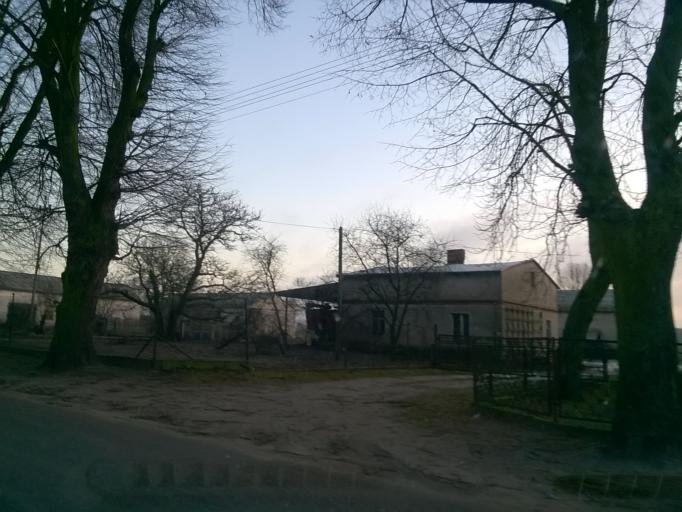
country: PL
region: Kujawsko-Pomorskie
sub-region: Powiat nakielski
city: Kcynia
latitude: 53.0259
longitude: 17.4239
